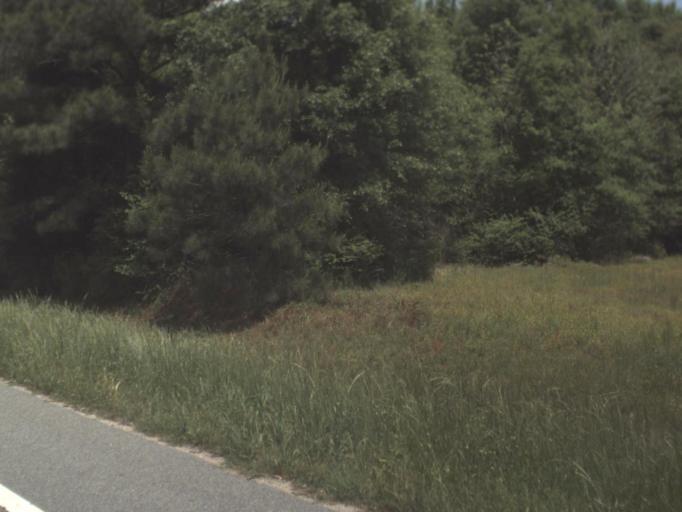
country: US
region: Alabama
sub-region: Escambia County
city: Atmore
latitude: 30.9570
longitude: -87.4860
